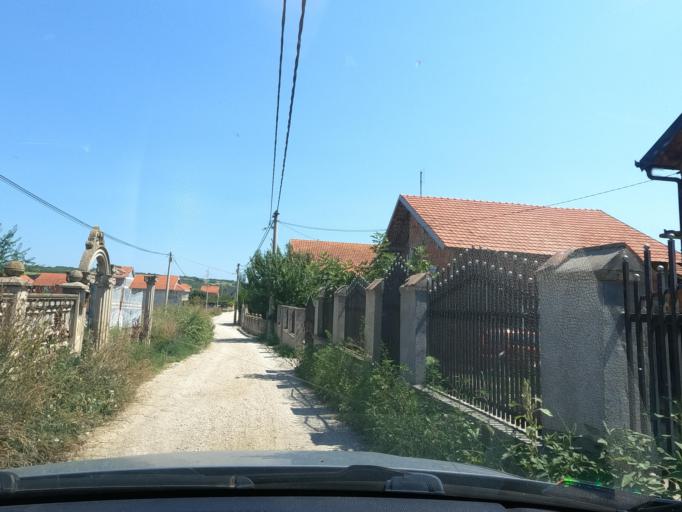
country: RS
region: Central Serbia
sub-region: Branicevski Okrug
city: Pozarevac
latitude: 44.7039
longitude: 21.1657
